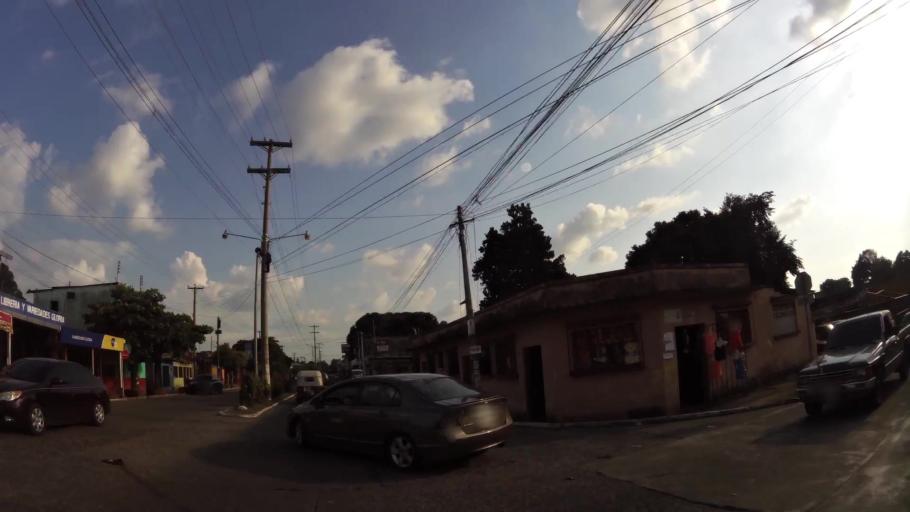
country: GT
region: Retalhuleu
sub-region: Municipio de Retalhuleu
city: Retalhuleu
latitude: 14.5427
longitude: -91.6772
